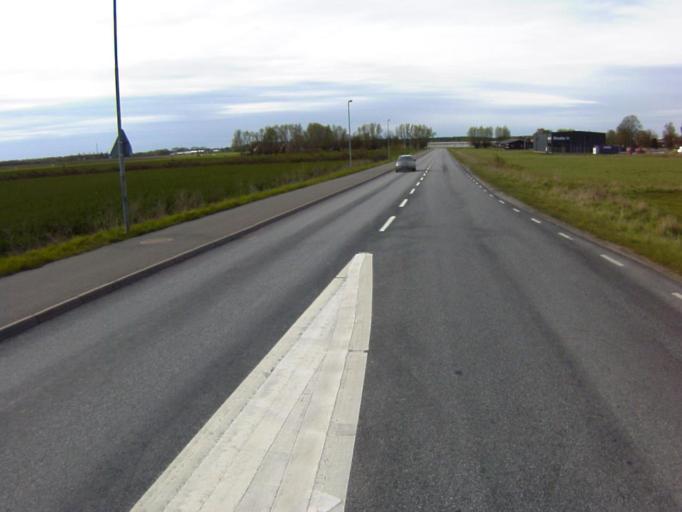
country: SE
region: Skane
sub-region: Kristianstads Kommun
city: Kristianstad
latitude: 56.0150
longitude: 14.1248
